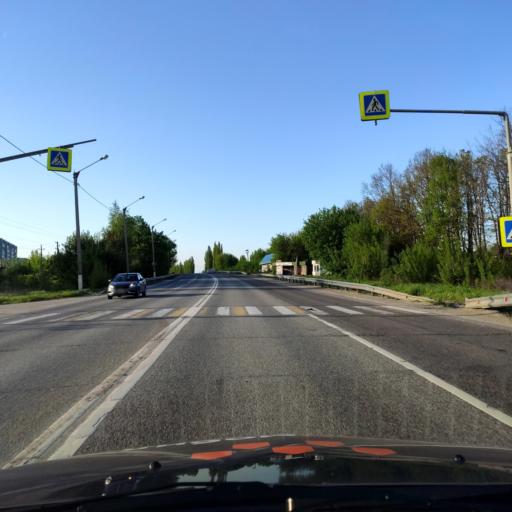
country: RU
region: Lipetsk
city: Yelets
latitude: 52.6129
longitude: 38.4618
